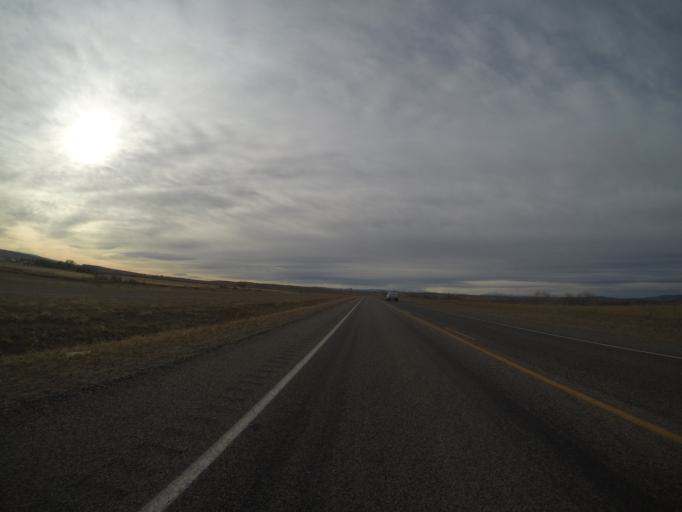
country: US
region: Montana
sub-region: Yellowstone County
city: Laurel
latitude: 45.6170
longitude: -108.8156
